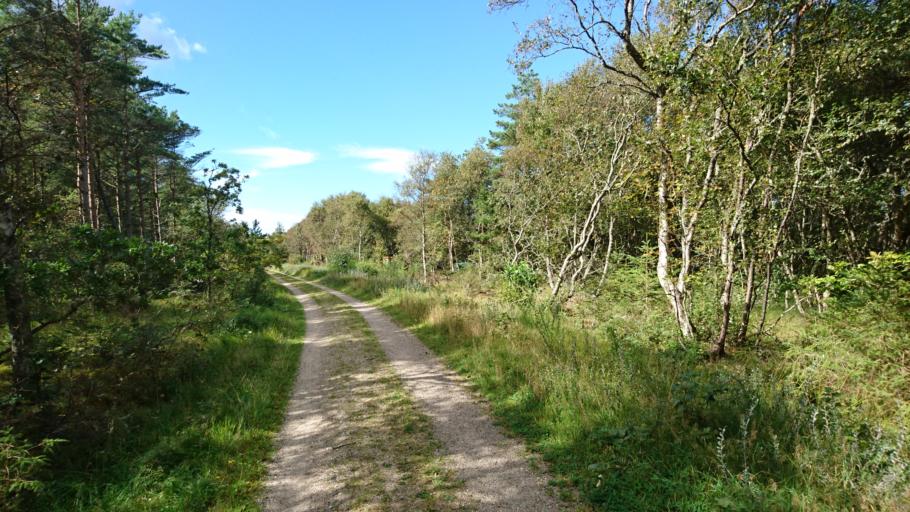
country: DK
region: North Denmark
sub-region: Frederikshavn Kommune
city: Skagen
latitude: 57.7157
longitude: 10.5204
